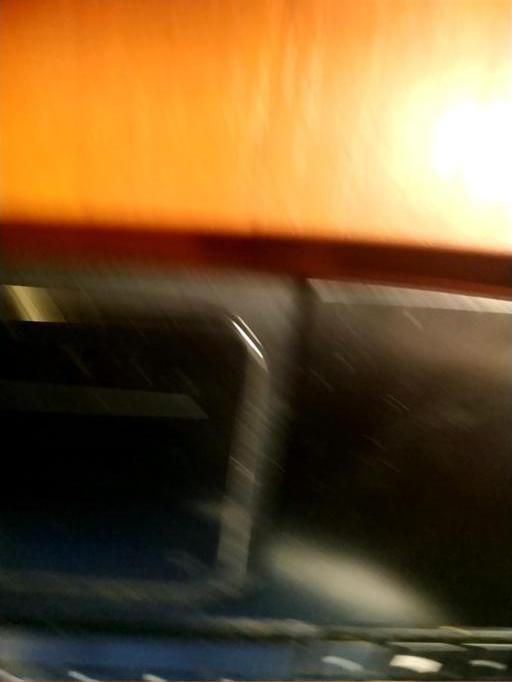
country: RU
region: Tverskaya
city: Rameshki
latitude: 57.2437
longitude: 35.9005
